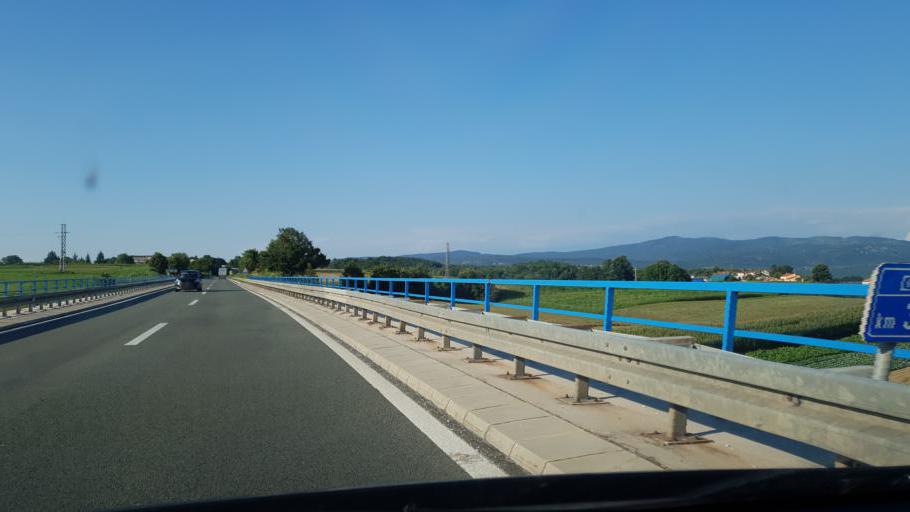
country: HR
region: Istarska
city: Buzet
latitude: 45.3063
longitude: 14.0620
